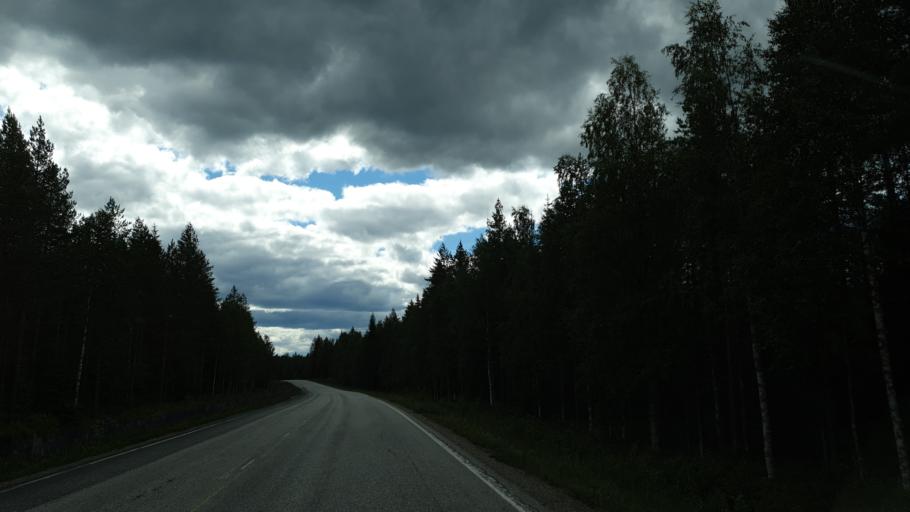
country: FI
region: Kainuu
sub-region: Kehys-Kainuu
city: Kuhmo
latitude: 63.9808
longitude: 29.6407
